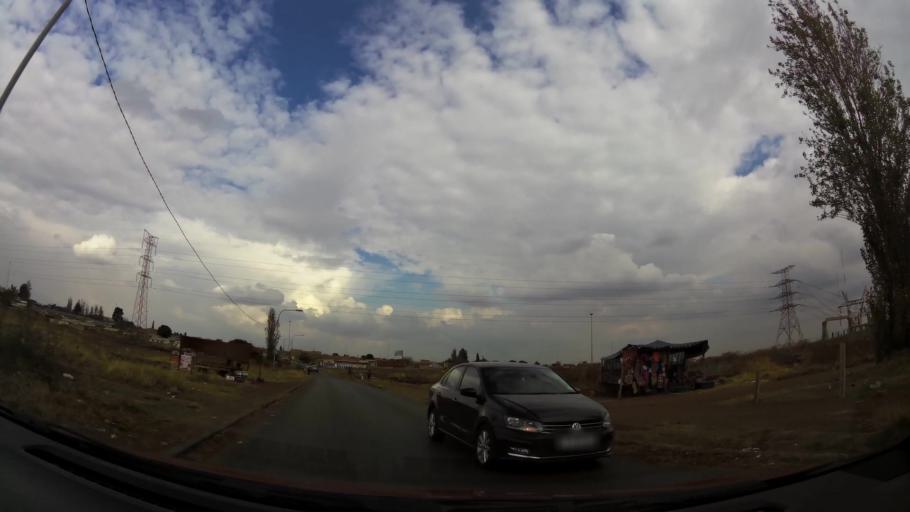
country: ZA
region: Gauteng
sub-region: City of Johannesburg Metropolitan Municipality
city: Soweto
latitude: -26.2406
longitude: 27.8488
